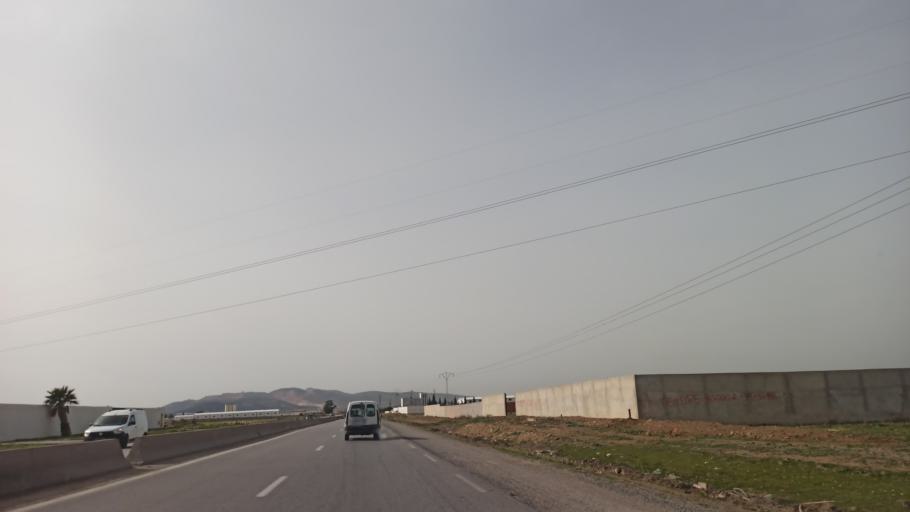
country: TN
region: Tunis
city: La Mohammedia
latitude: 36.5728
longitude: 10.0881
